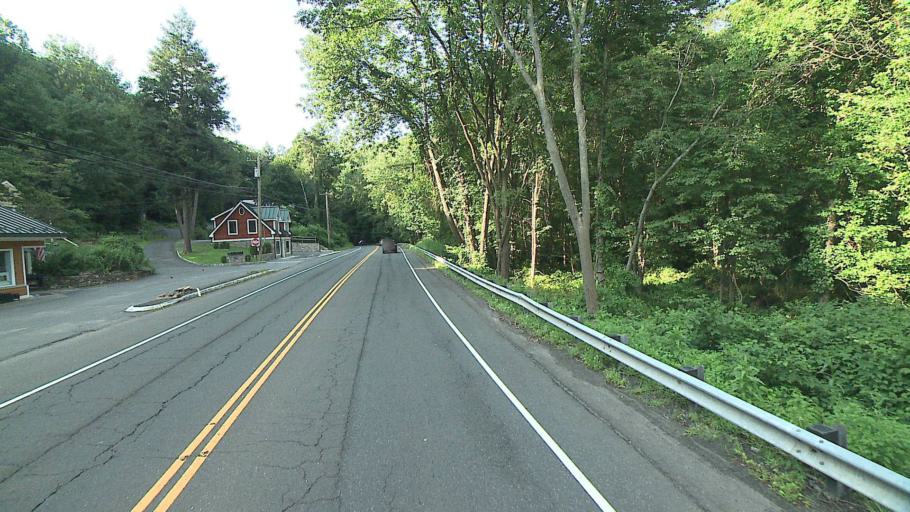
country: US
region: Connecticut
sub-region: Fairfield County
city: Georgetown
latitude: 41.2520
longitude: -73.4341
